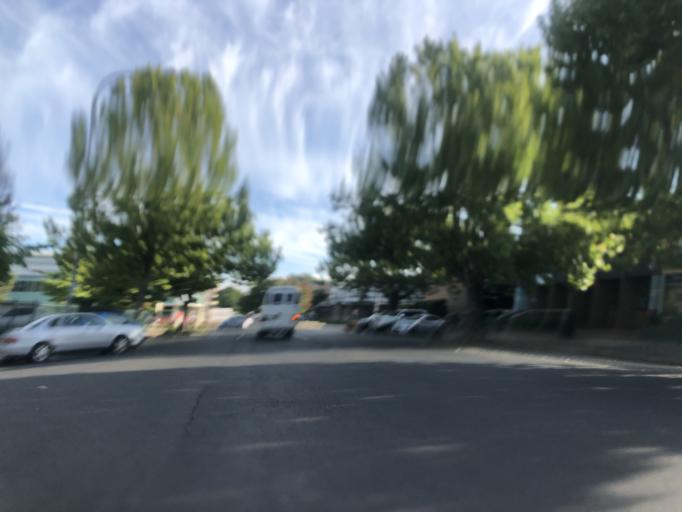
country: AU
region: New South Wales
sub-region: Orange Municipality
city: Orange
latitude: -33.2866
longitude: 149.1005
